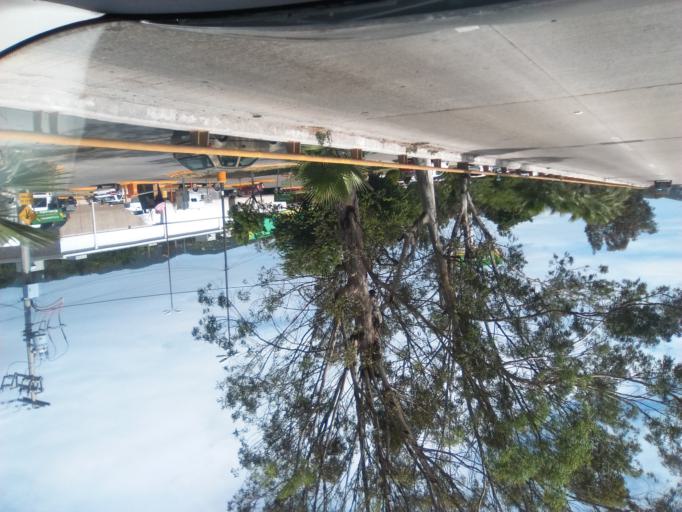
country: MX
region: Guerrero
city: Chilpancingo de los Bravos
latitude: 17.5310
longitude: -99.4933
